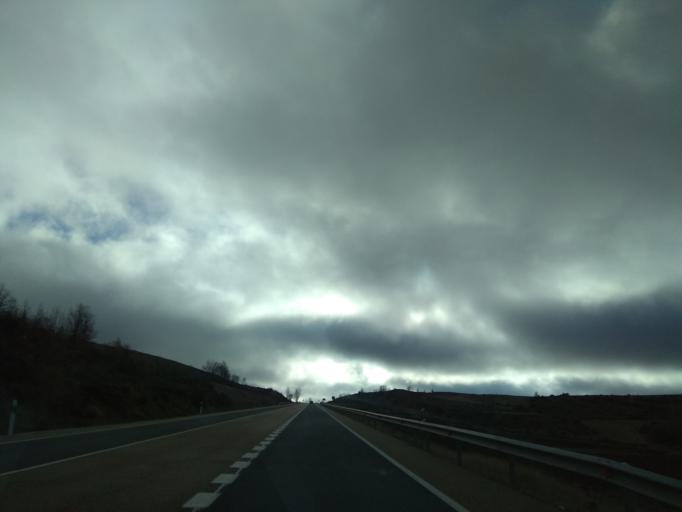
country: ES
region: Castille and Leon
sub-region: Provincia de Burgos
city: Huermeces
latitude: 42.5538
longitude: -3.7457
